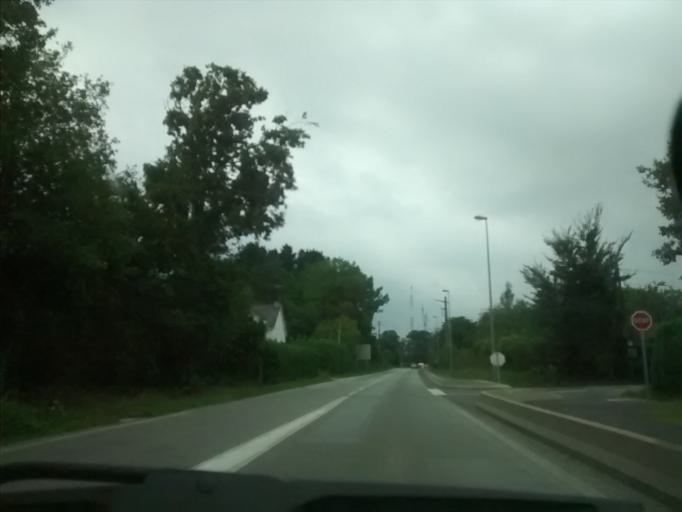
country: FR
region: Brittany
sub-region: Departement du Morbihan
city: Guer
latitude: 47.9126
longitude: -2.1234
